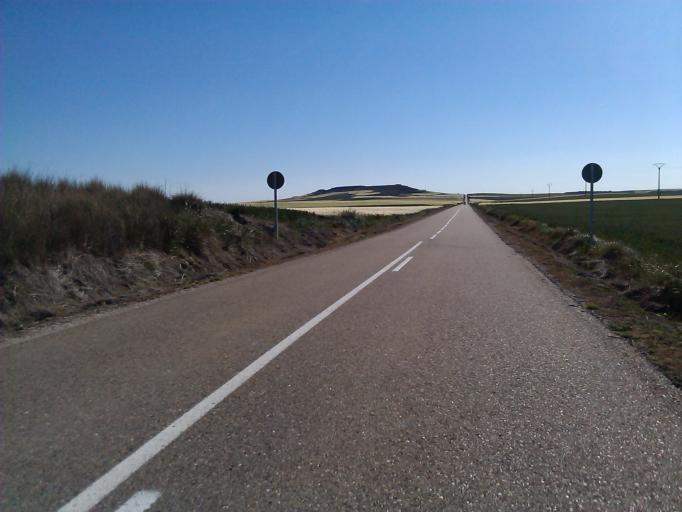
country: ES
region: Castille and Leon
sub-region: Provincia de Burgos
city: Pedrosa del Principe
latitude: 42.3035
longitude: -4.1905
